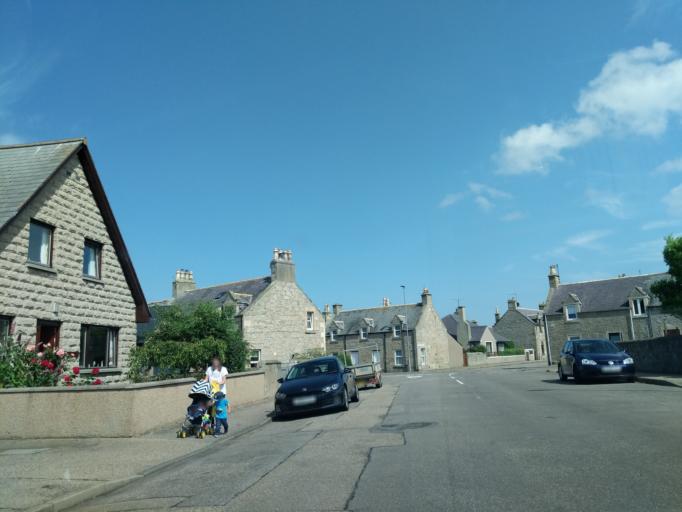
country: GB
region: Scotland
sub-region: Moray
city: Lossiemouth
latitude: 57.7235
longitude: -3.2899
